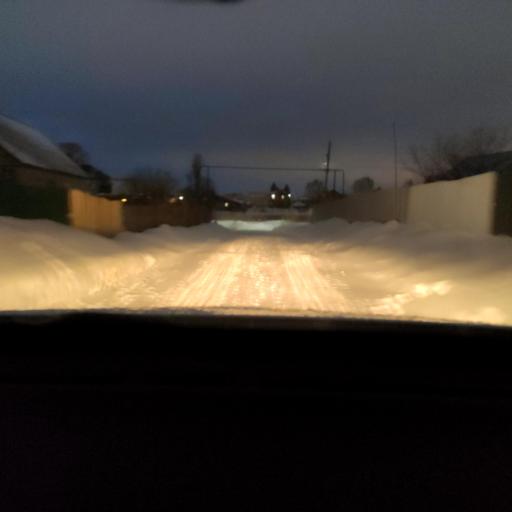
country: RU
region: Tatarstan
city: Stolbishchi
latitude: 55.6949
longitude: 49.1519
